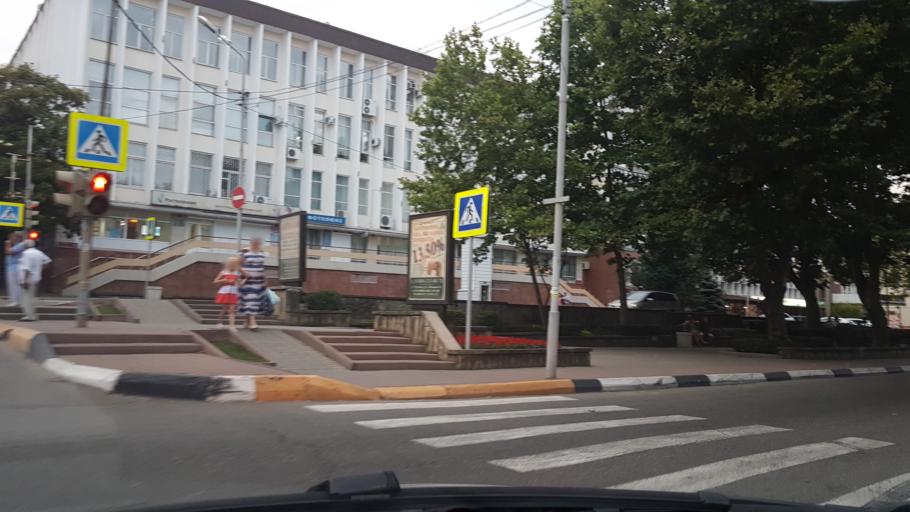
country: RU
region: Krasnodarskiy
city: Tuapse
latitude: 44.0973
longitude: 39.0765
